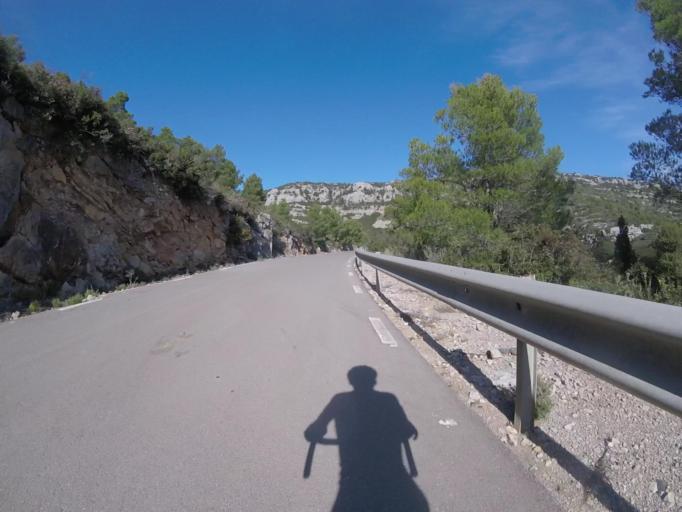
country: ES
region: Valencia
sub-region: Provincia de Castello
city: Sarratella
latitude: 40.2718
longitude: 0.0492
